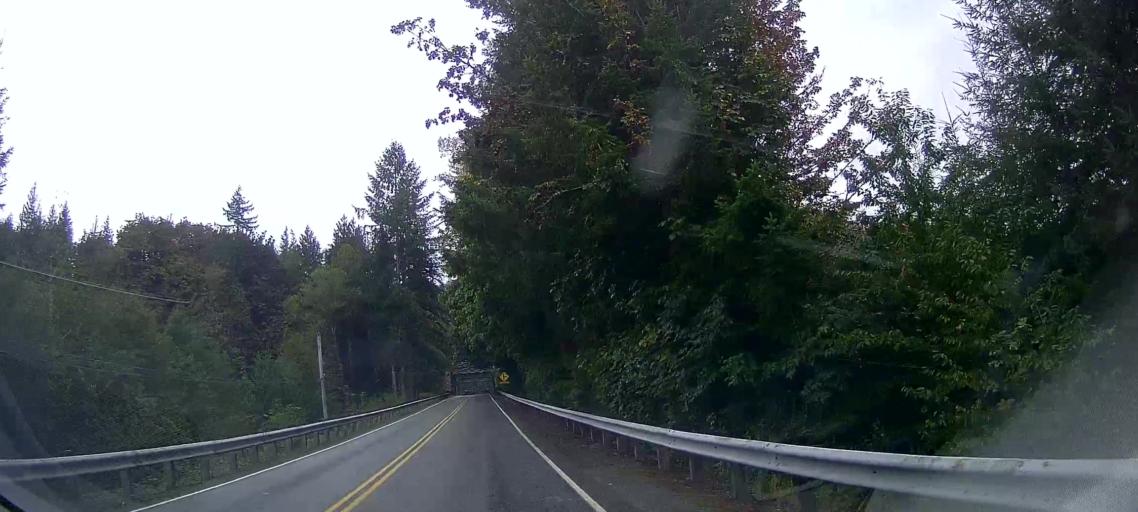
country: US
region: Washington
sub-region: Snohomish County
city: Darrington
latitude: 48.5260
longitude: -121.7693
